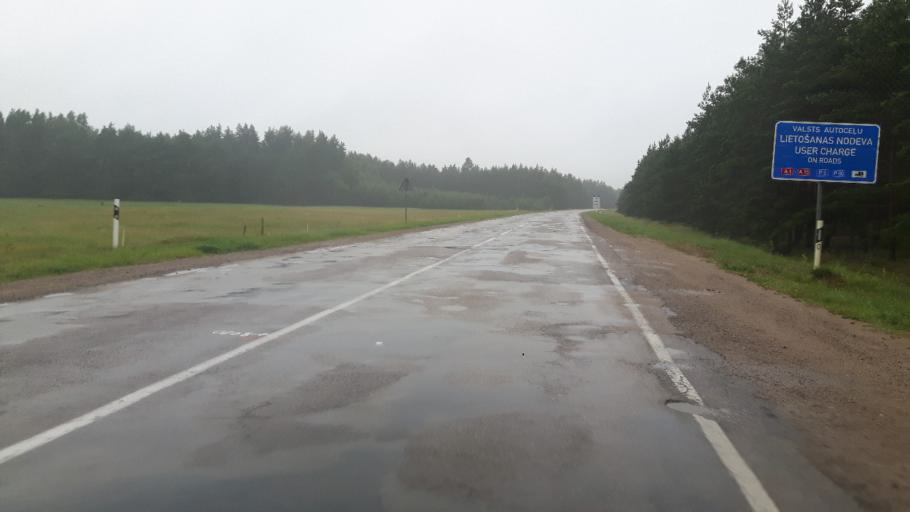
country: LT
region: Klaipedos apskritis
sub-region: Palanga
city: Sventoji
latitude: 56.0813
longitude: 21.1229
